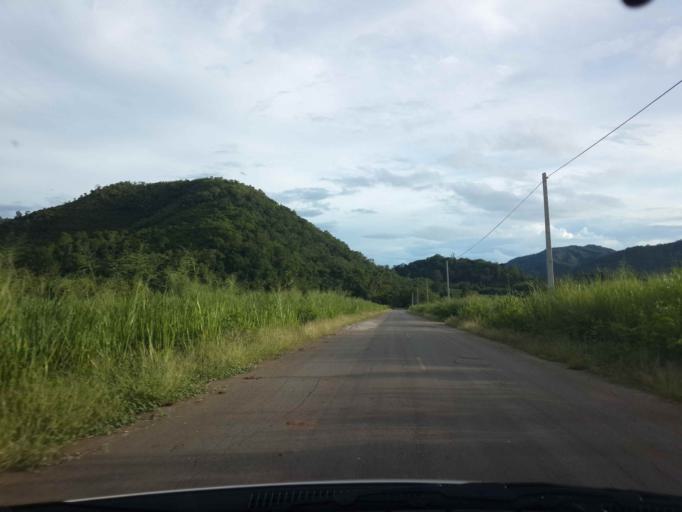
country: TH
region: Kanchanaburi
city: Dan Makham Tia
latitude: 13.7669
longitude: 99.2015
